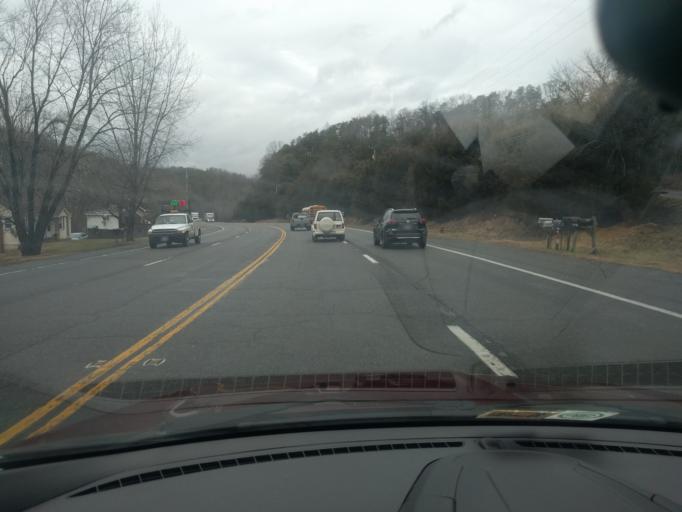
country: US
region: Virginia
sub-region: Botetourt County
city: Fincastle
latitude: 37.5085
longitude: -79.8778
